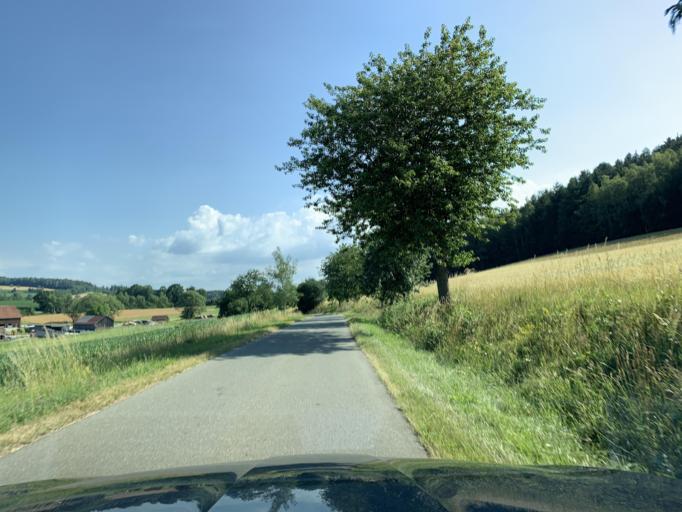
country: DE
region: Bavaria
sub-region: Upper Palatinate
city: Dieterskirchen
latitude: 49.4089
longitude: 12.4264
